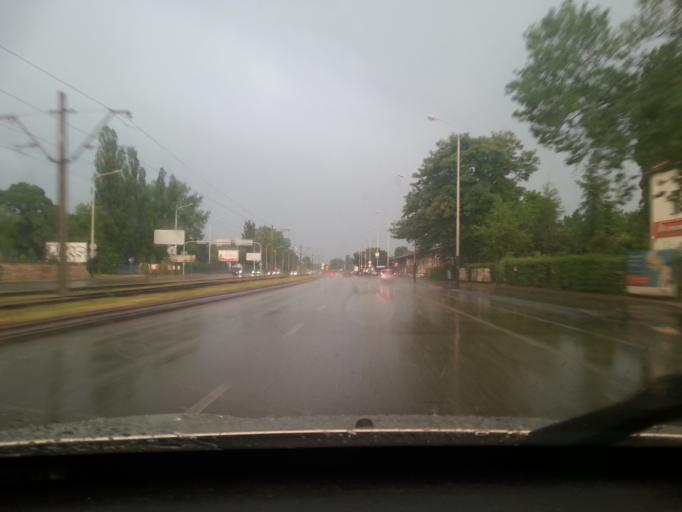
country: PL
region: Lodz Voivodeship
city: Lodz
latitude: 51.7673
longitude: 19.4265
